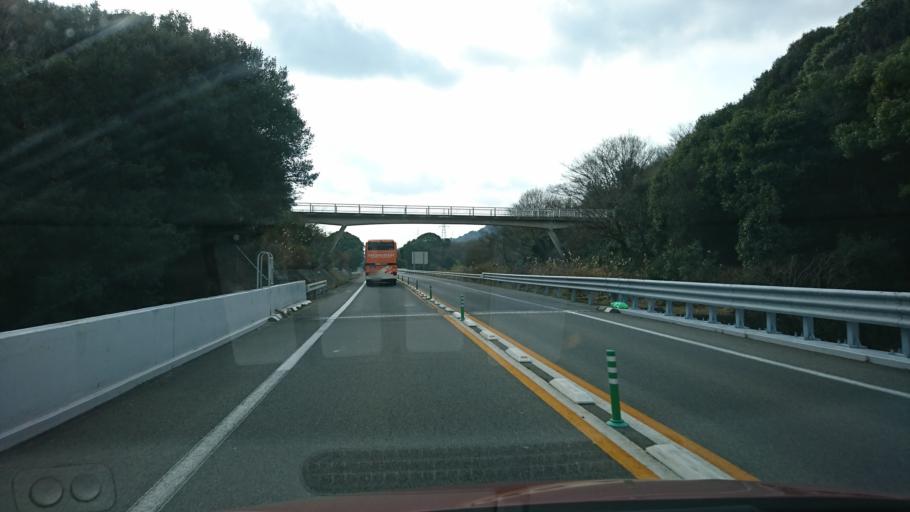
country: JP
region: Hiroshima
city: Innoshima
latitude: 34.2455
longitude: 133.0481
